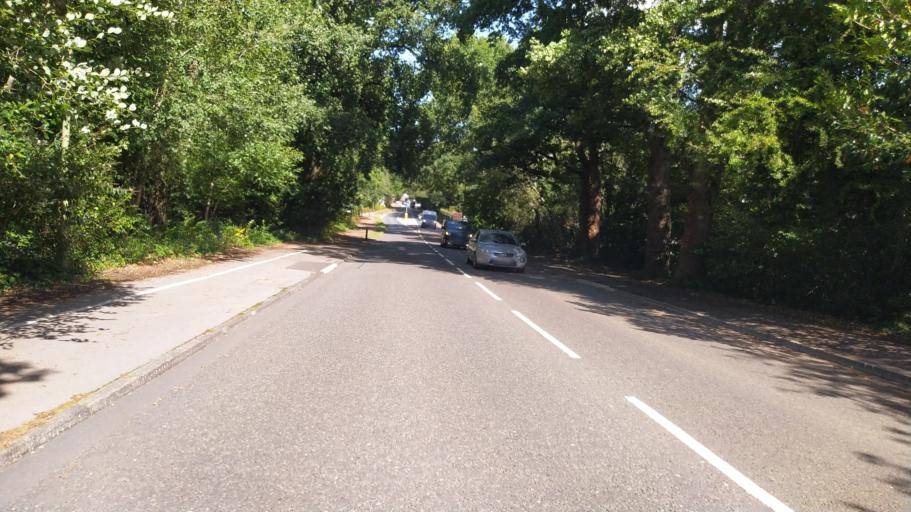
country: GB
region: England
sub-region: Hampshire
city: Bordon
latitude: 51.1040
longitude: -0.8679
